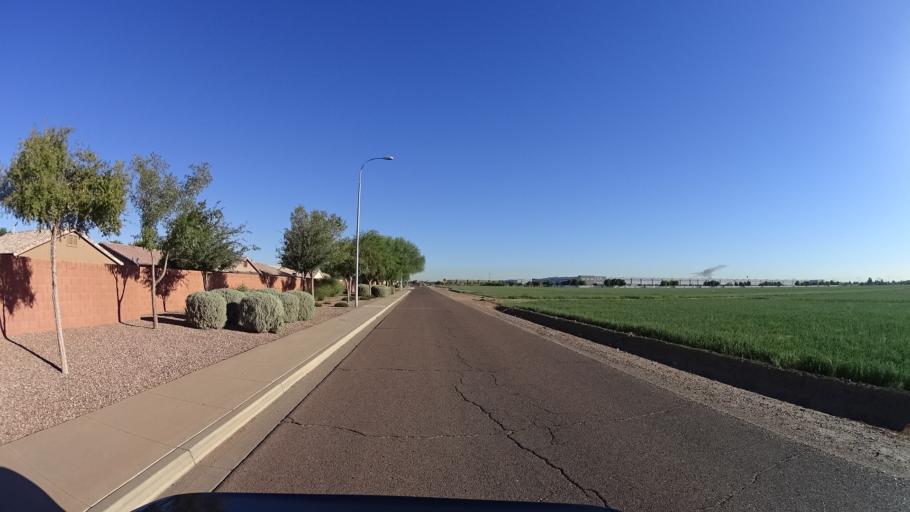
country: US
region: Arizona
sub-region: Maricopa County
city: Tolleson
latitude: 33.4277
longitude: -112.2127
